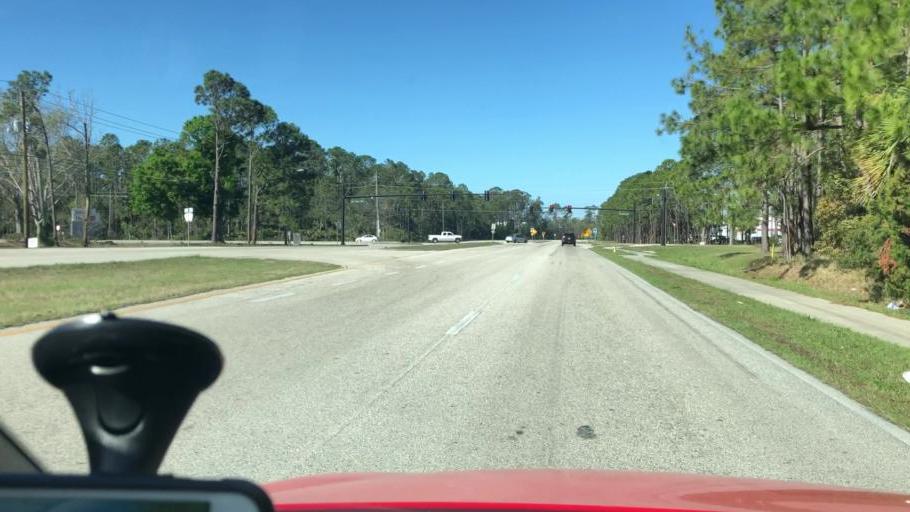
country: US
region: Florida
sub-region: Volusia County
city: Holly Hill
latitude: 29.2095
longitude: -81.0729
